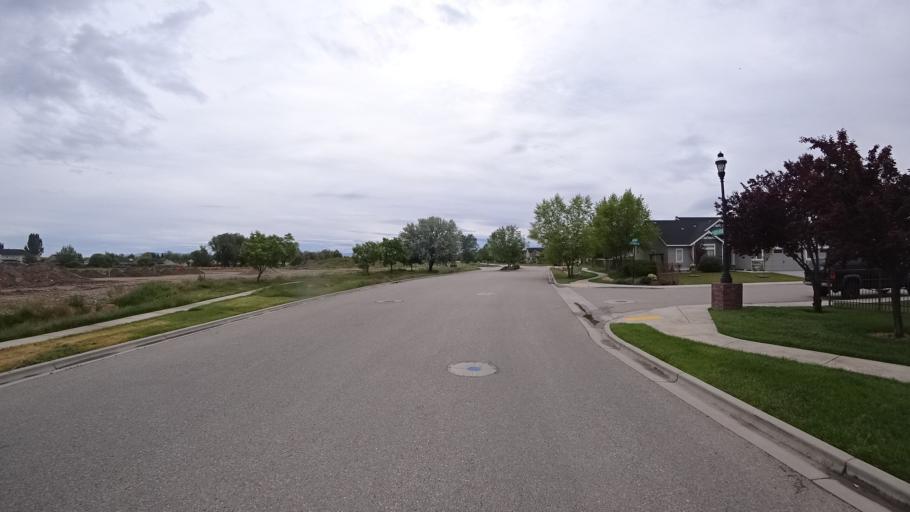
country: US
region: Idaho
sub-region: Ada County
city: Star
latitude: 43.7013
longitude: -116.4990
